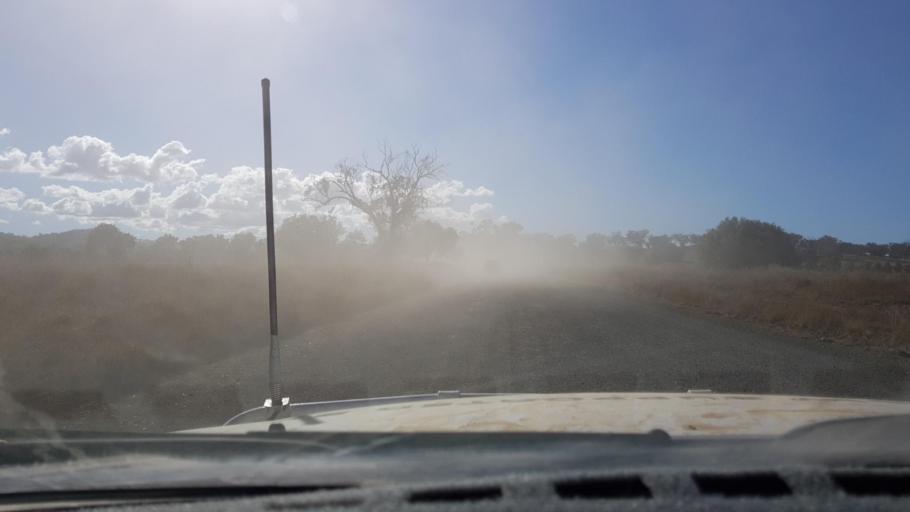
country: AU
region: New South Wales
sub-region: Narrabri
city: Blair Athol
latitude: -30.6673
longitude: 150.4609
